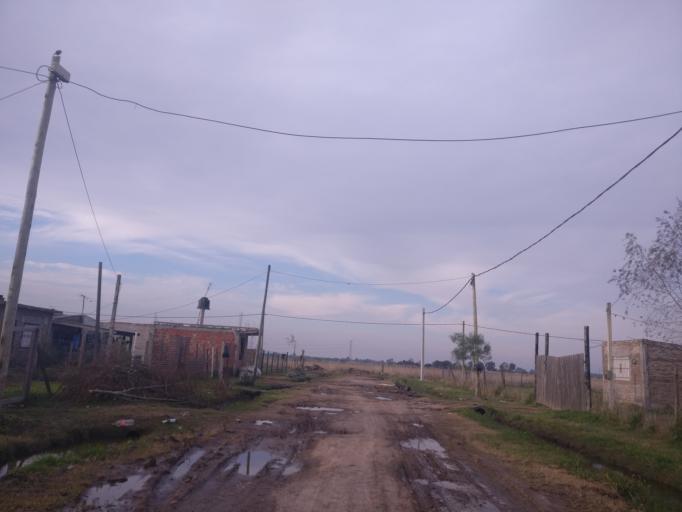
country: AR
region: Buenos Aires
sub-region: Partido de Ezeiza
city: Ezeiza
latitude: -34.9361
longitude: -58.6052
